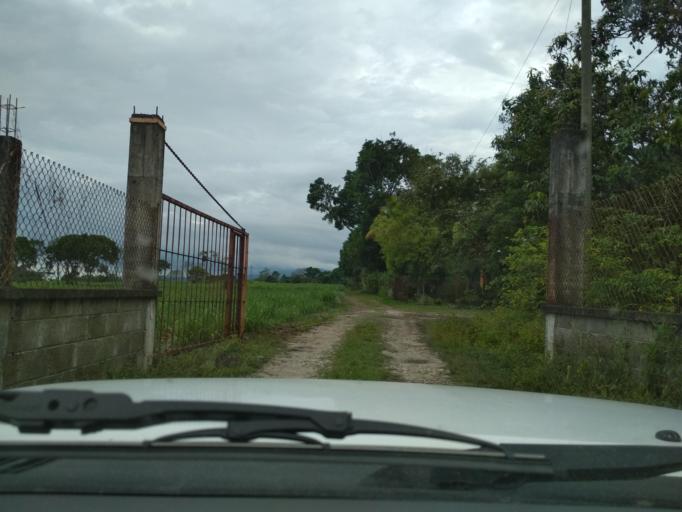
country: MX
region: Veracruz
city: Paraje Nuevo
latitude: 18.8719
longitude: -96.8558
